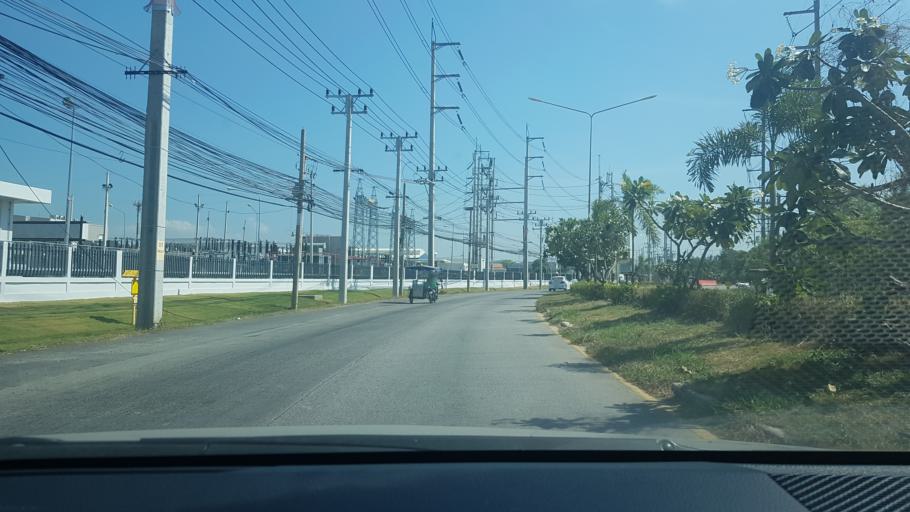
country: TH
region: Phra Nakhon Si Ayutthaya
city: Bang Pa-in
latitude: 14.2524
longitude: 100.6020
